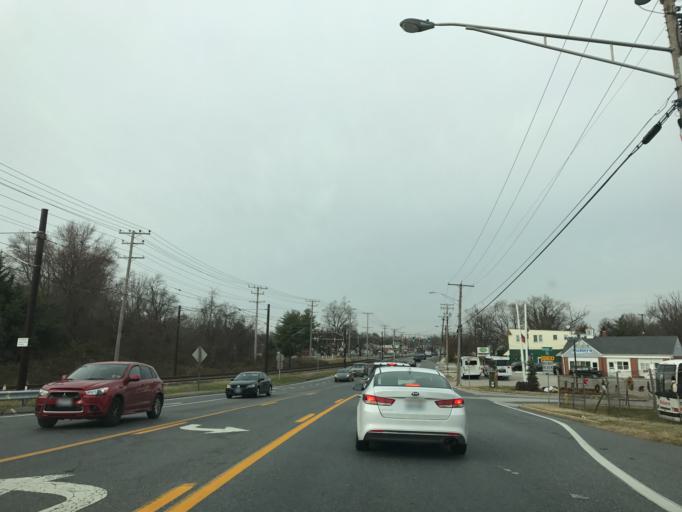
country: US
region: Maryland
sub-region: Anne Arundel County
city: Ferndale
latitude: 39.1786
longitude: -76.6380
